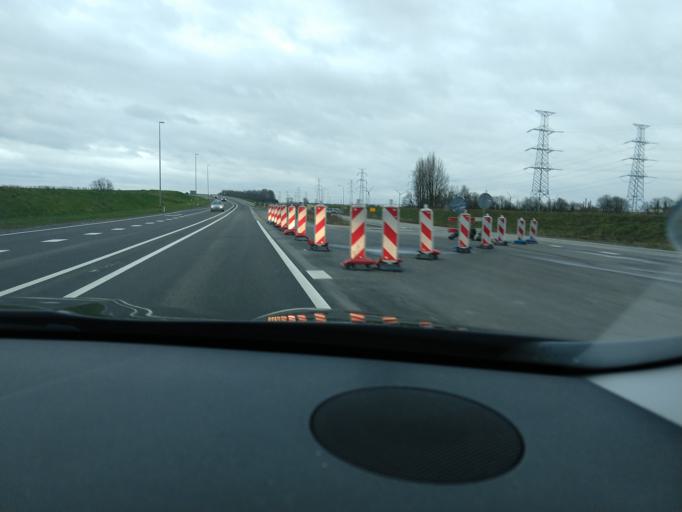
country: NL
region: Zeeland
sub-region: Gemeente Borsele
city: Borssele
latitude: 51.4621
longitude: 3.7364
